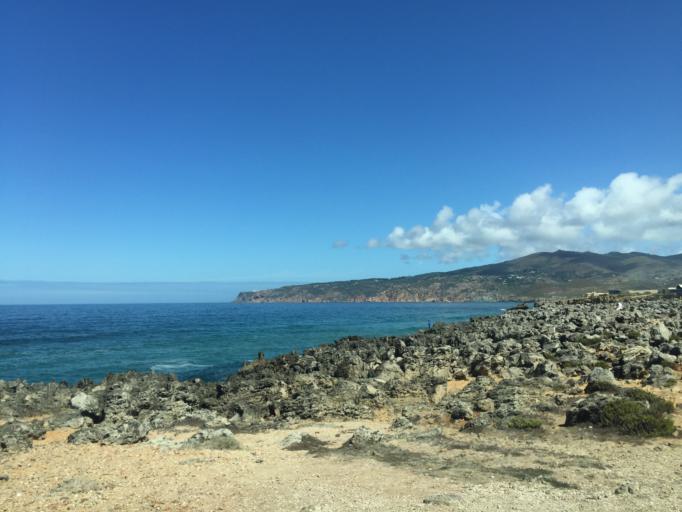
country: PT
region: Lisbon
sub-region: Cascais
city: Cascais
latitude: 38.7172
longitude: -9.4813
